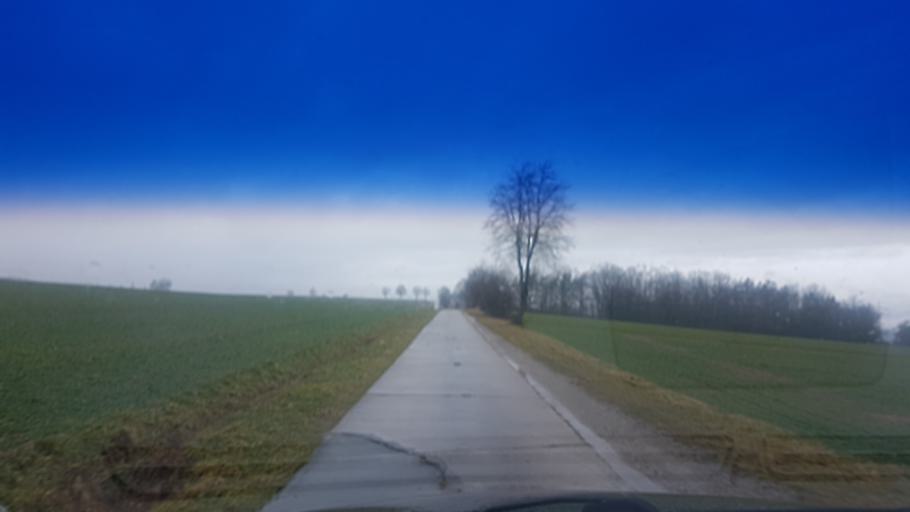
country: DE
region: Bavaria
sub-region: Upper Franconia
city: Burgebrach
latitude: 49.8054
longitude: 10.7729
